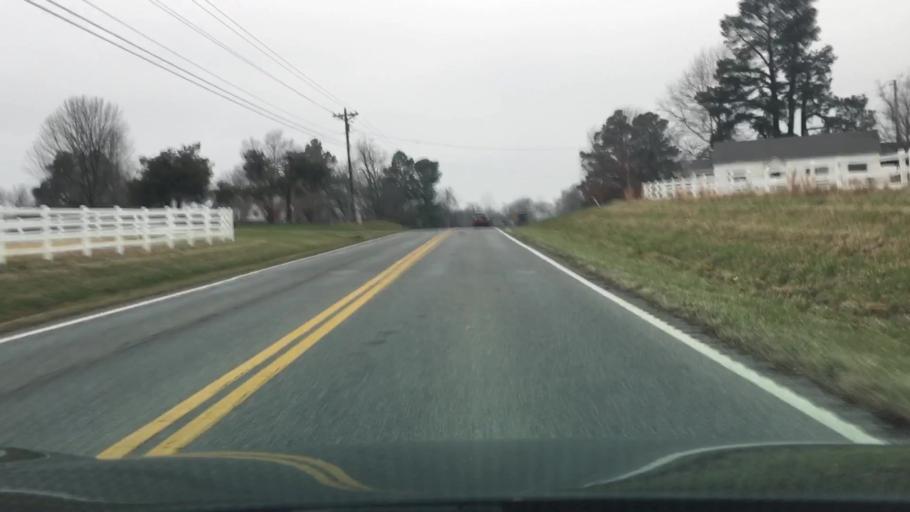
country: US
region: Kentucky
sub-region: Livingston County
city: Ledbetter
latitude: 36.9666
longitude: -88.4358
